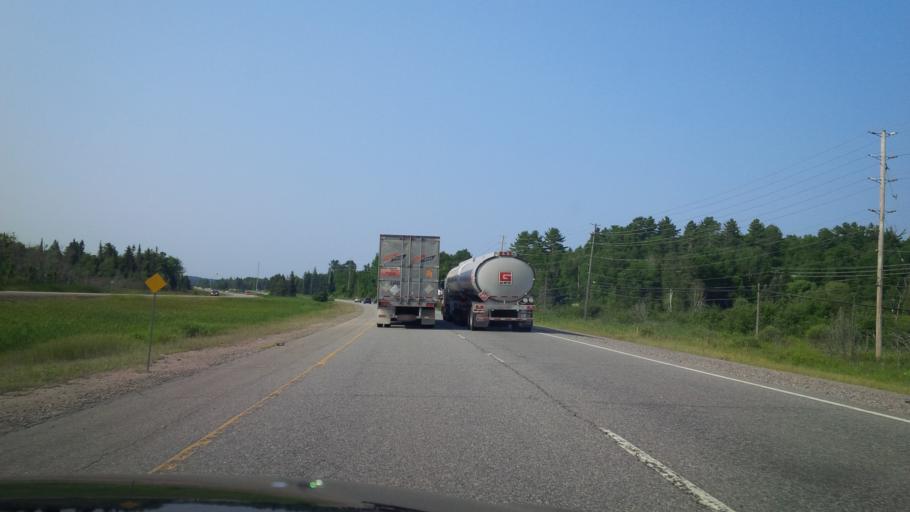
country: CA
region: Ontario
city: Huntsville
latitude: 45.2609
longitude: -79.2948
